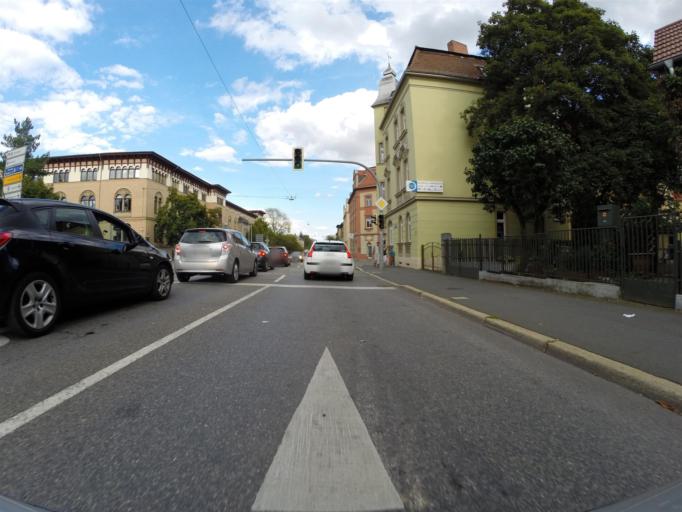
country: DE
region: Thuringia
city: Weimar
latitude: 50.9808
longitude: 11.3158
